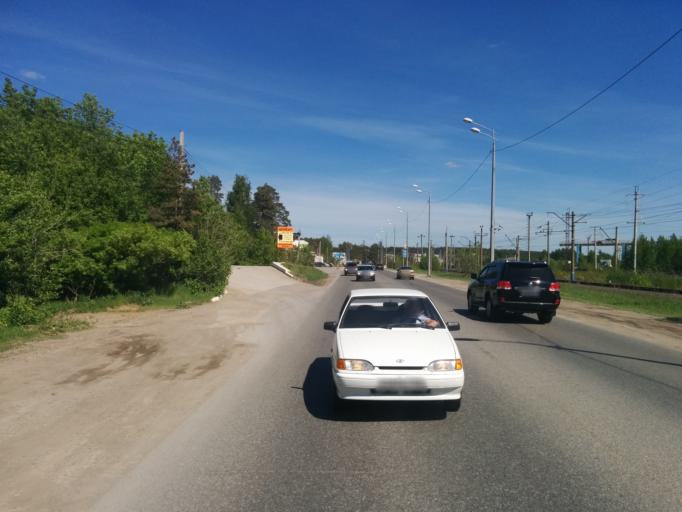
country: RU
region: Perm
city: Kondratovo
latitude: 58.0360
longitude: 56.1550
